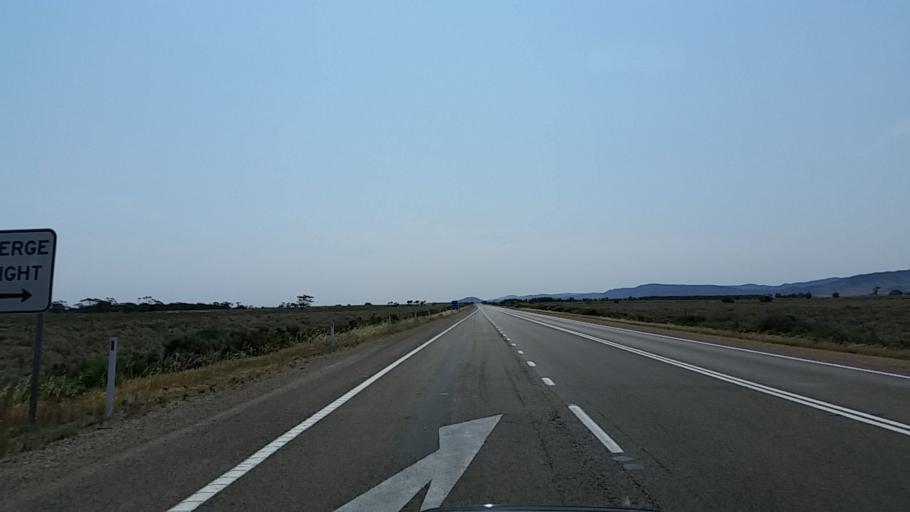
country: AU
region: South Australia
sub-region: Port Pirie City and Dists
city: Port Pirie
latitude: -32.9712
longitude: 137.9825
